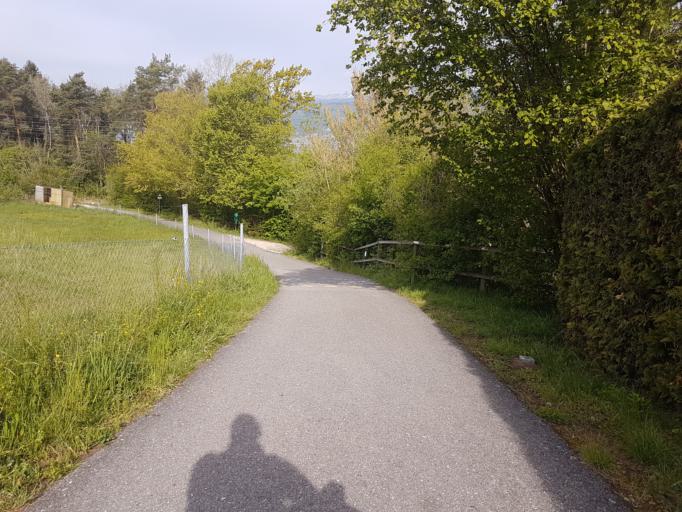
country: CH
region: Bern
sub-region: Seeland District
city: Tauffelen
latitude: 47.0839
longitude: 7.2044
